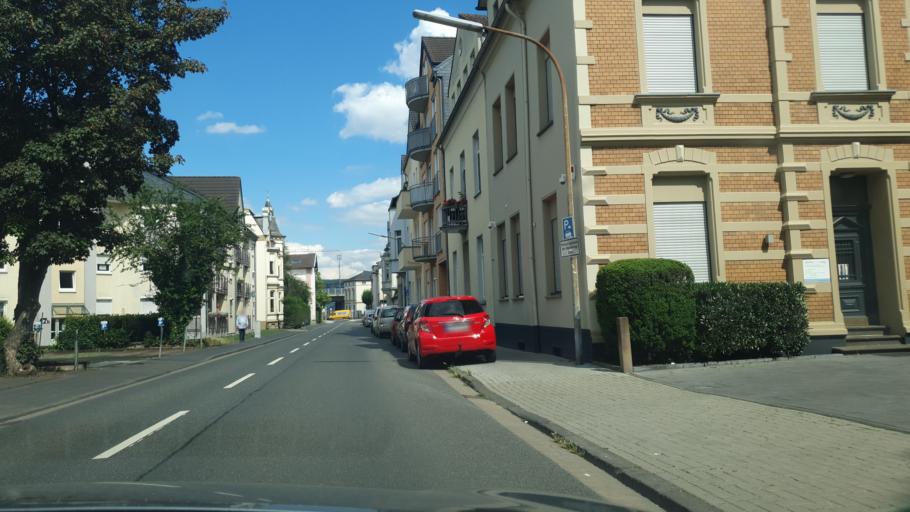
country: DE
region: Rheinland-Pfalz
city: Sinzig
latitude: 50.5461
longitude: 7.2544
